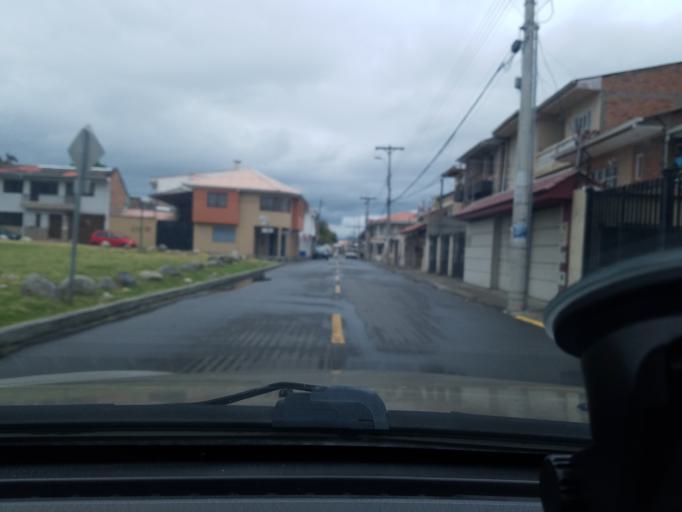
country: EC
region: Azuay
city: Cuenca
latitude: -2.9078
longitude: -78.9924
